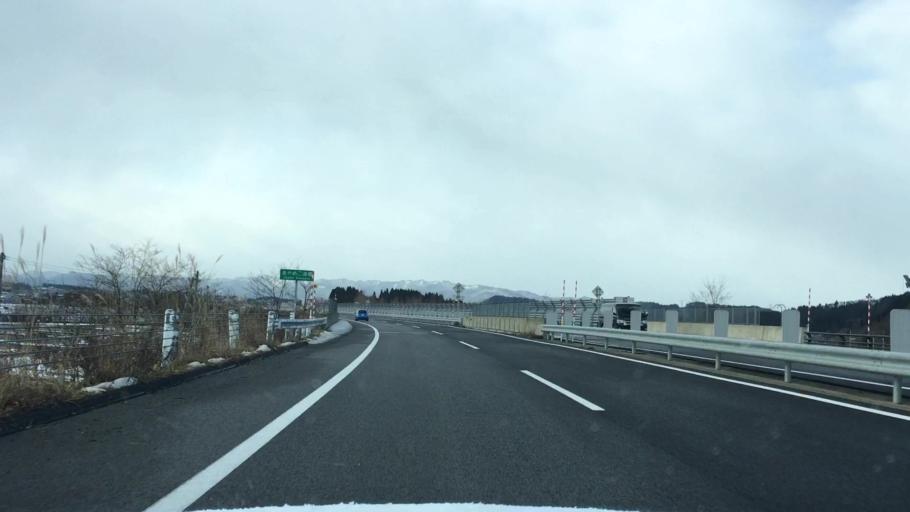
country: JP
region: Akita
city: Odate
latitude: 40.3002
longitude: 140.5565
